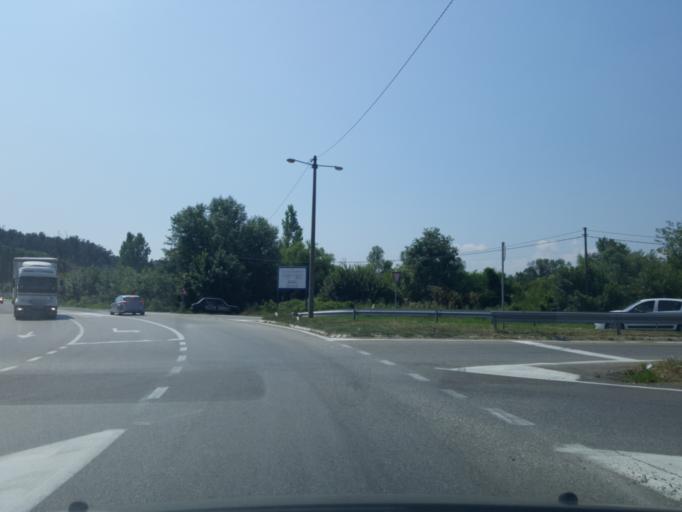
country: RS
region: Central Serbia
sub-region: Belgrade
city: Mladenovac
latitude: 44.4935
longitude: 20.6562
